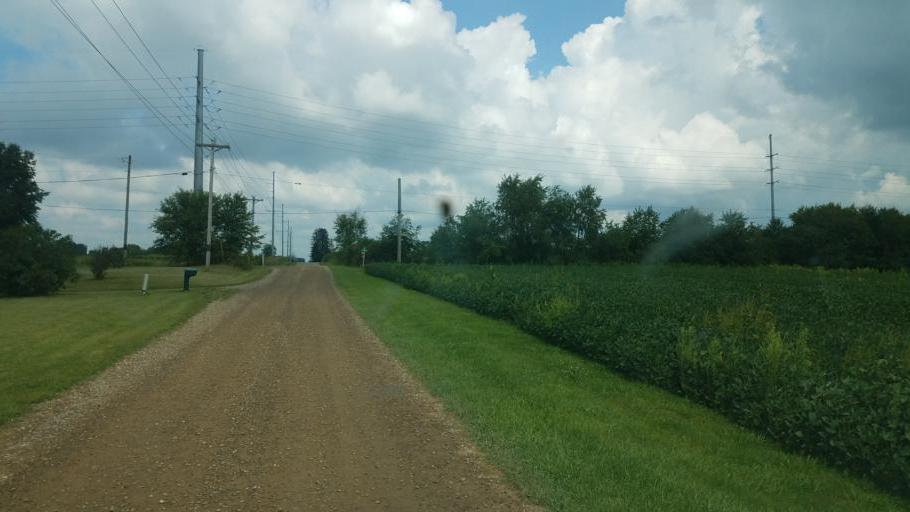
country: US
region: Ohio
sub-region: Knox County
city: Mount Vernon
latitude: 40.3369
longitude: -82.4854
